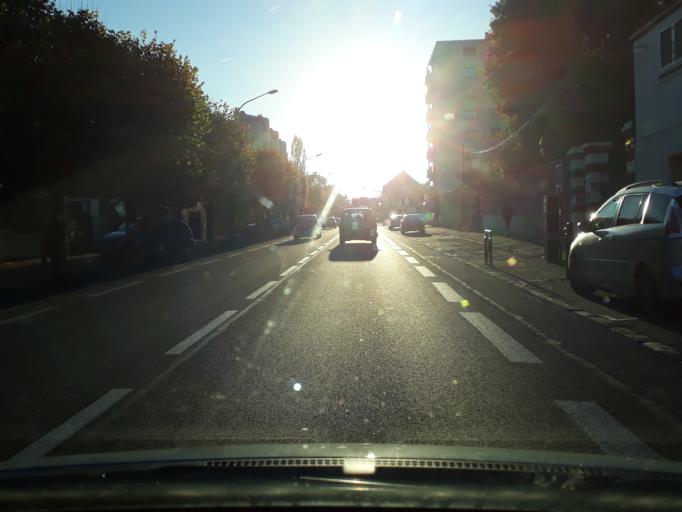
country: FR
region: Ile-de-France
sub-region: Departement de Seine-et-Marne
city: Avon
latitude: 48.4186
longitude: 2.7310
